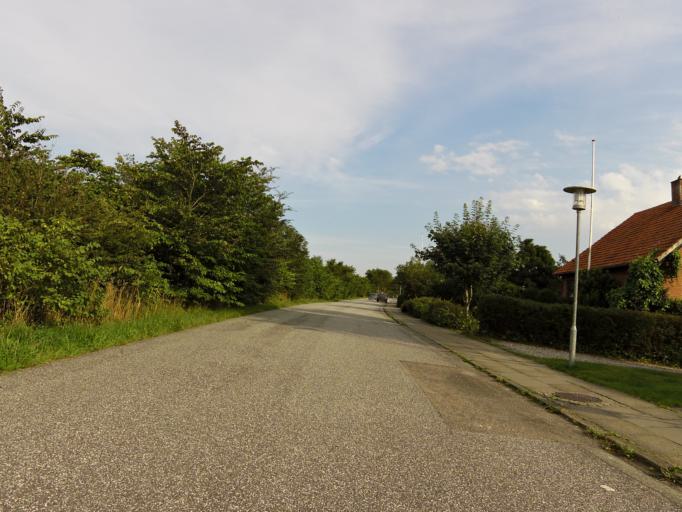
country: DK
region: South Denmark
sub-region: Esbjerg Kommune
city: Ribe
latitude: 55.3251
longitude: 8.7600
